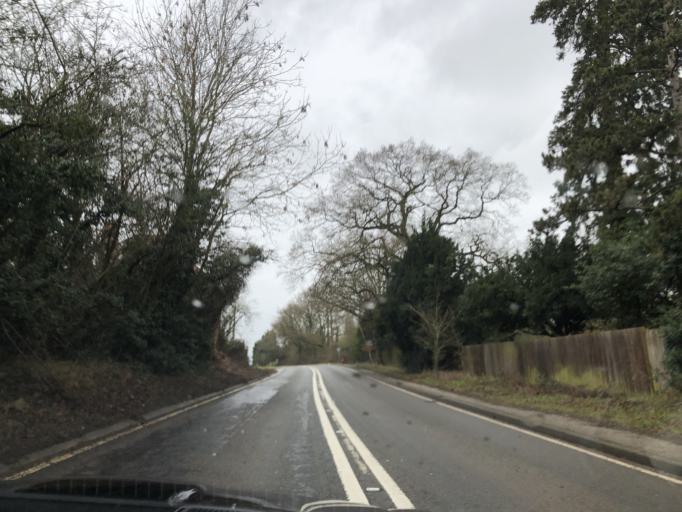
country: GB
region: England
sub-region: Warwickshire
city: Henley in Arden
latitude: 52.2852
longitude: -1.7544
